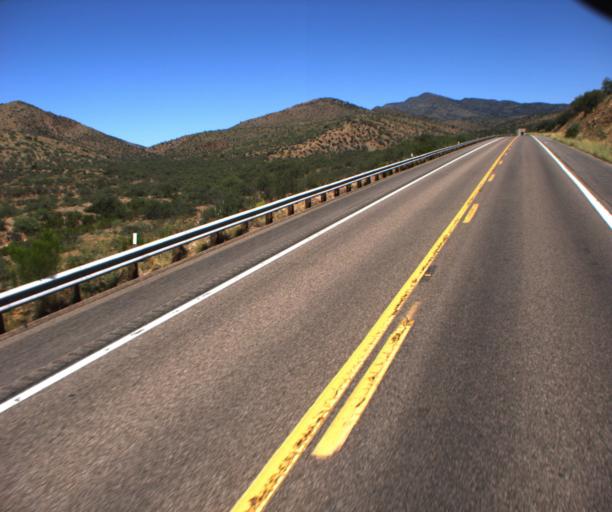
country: US
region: Arizona
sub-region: Gila County
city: Globe
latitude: 33.4527
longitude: -110.7208
